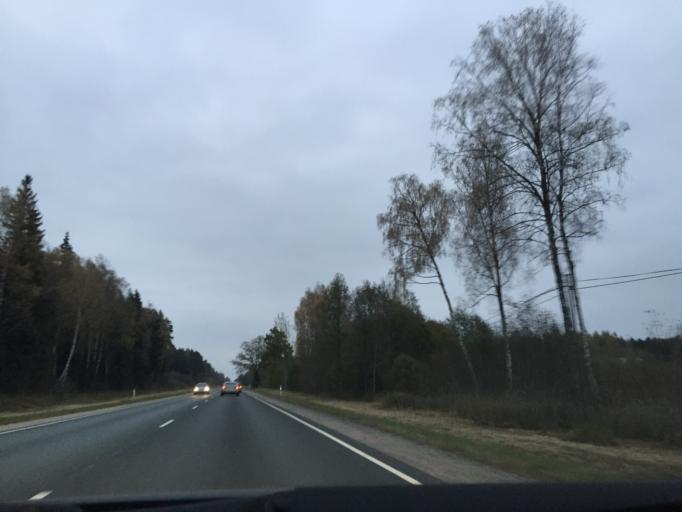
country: LV
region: Ozolnieku
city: Ozolnieki
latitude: 56.7111
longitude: 23.8286
